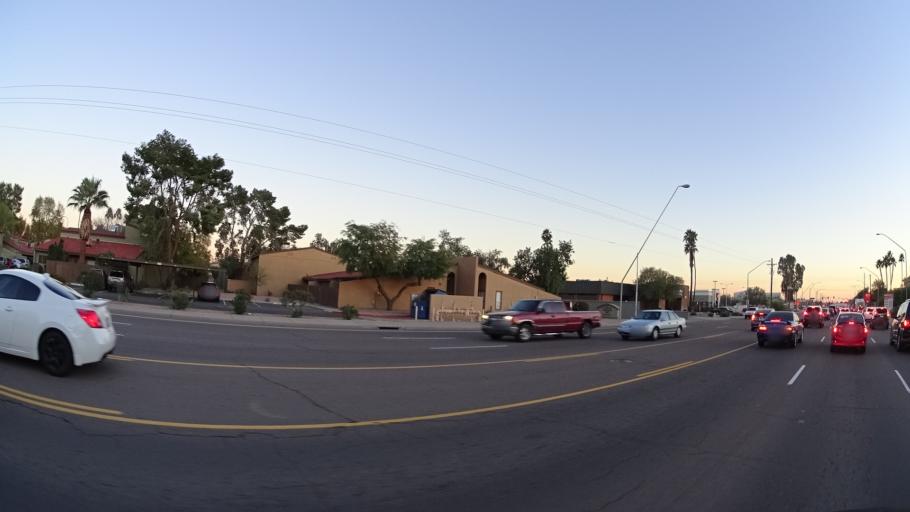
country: US
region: Arizona
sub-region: Maricopa County
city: Tempe
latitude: 33.3954
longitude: -111.8748
